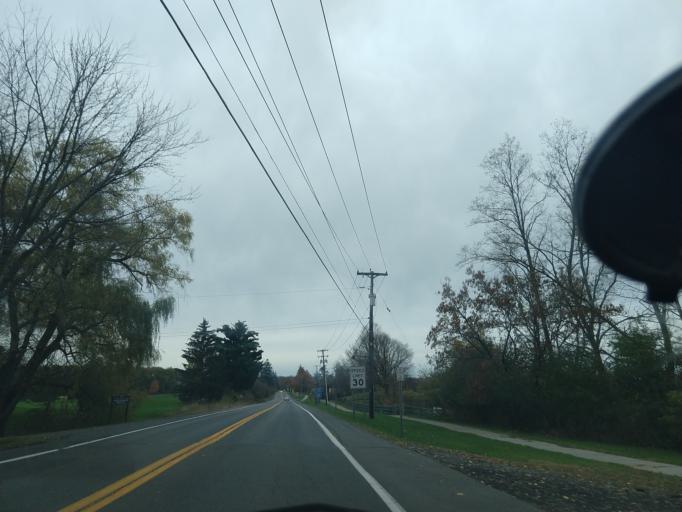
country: US
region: New York
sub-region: Tompkins County
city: Cayuga Heights
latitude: 42.4604
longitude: -76.4756
